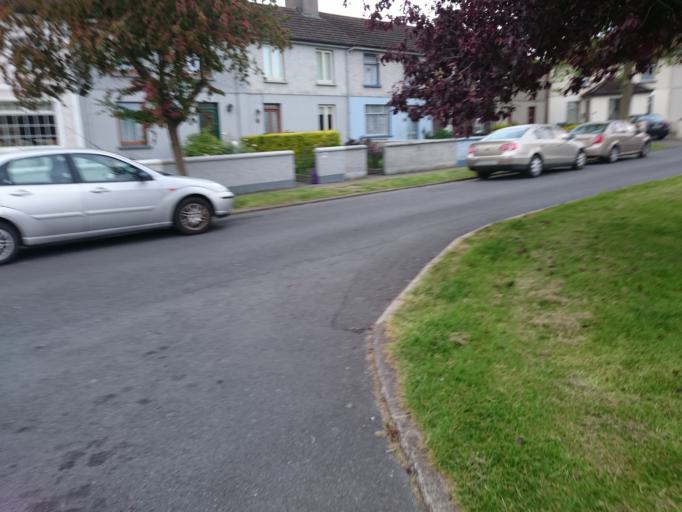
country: IE
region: Leinster
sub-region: Kilkenny
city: Kilkenny
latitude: 52.6504
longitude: -7.2636
